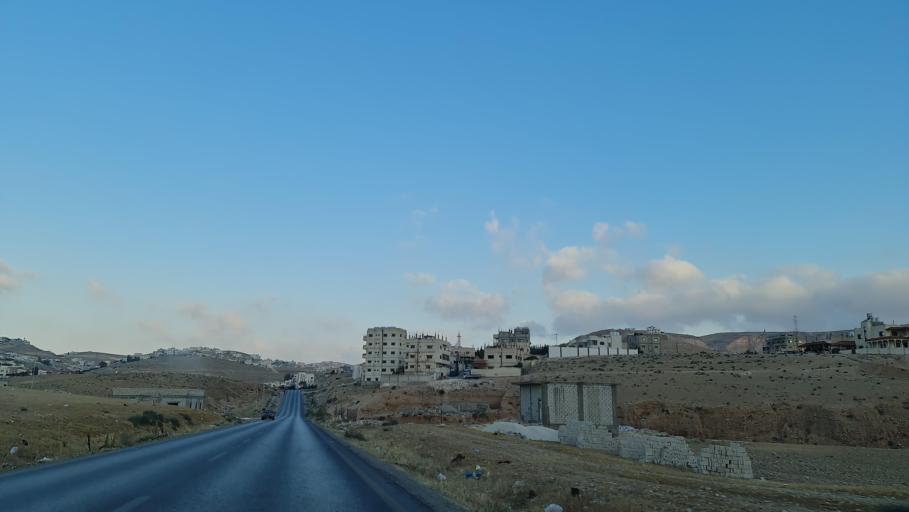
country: JO
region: Zarqa
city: Zarqa
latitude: 32.0822
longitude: 36.0633
